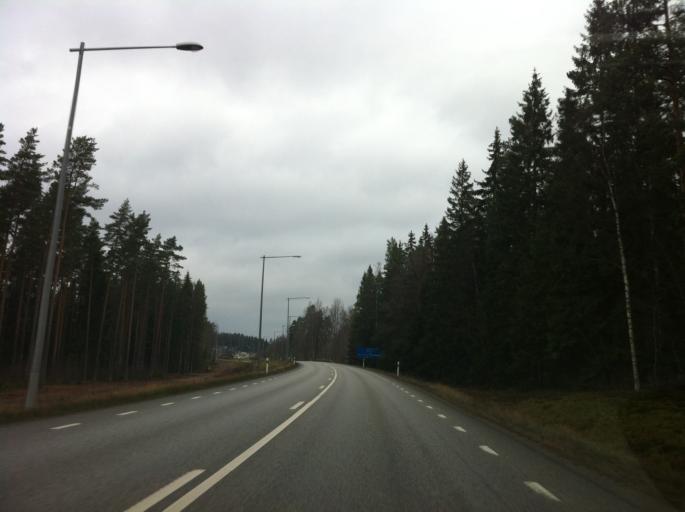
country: SE
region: Joenkoeping
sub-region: Vetlanda Kommun
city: Vetlanda
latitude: 57.4158
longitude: 15.0590
